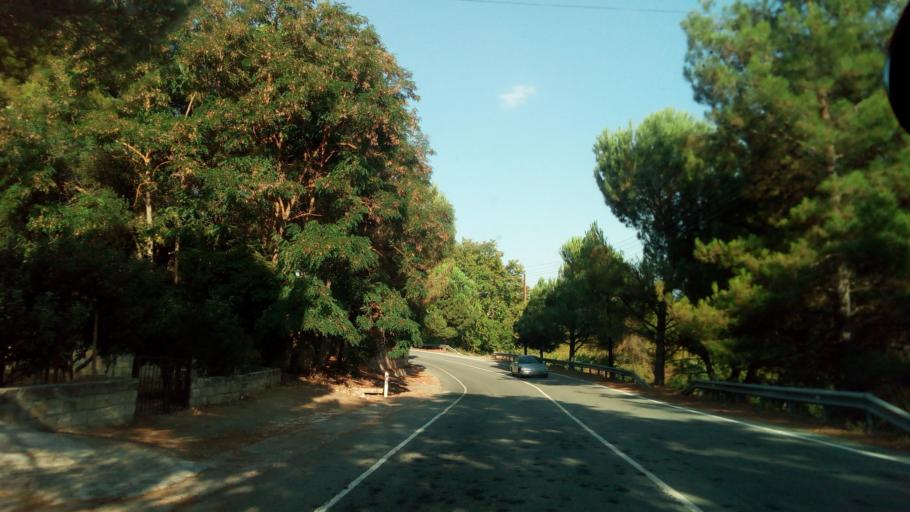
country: CY
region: Limassol
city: Pachna
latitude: 34.8692
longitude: 32.8379
